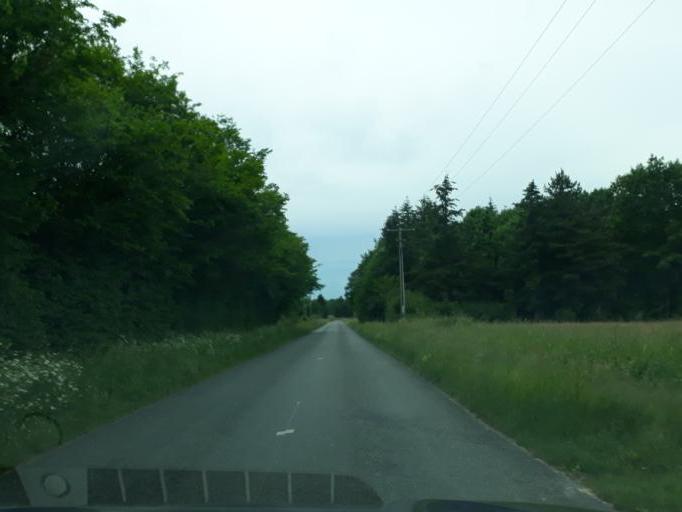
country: FR
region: Centre
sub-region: Departement du Loiret
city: Tigy
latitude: 47.7463
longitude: 2.2515
